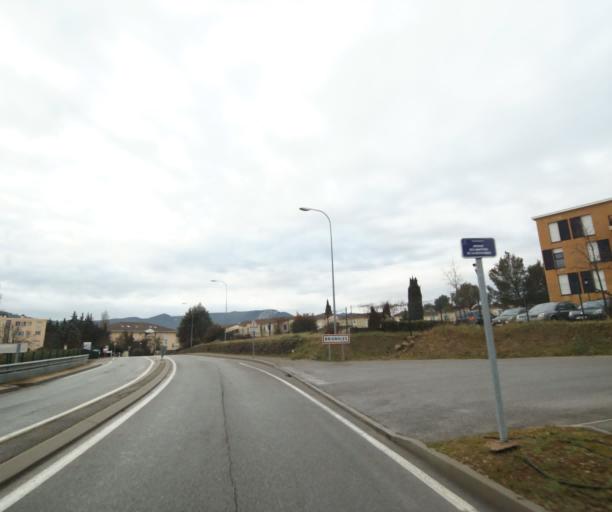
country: FR
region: Provence-Alpes-Cote d'Azur
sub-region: Departement du Var
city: Brignoles
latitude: 43.4140
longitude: 6.0685
